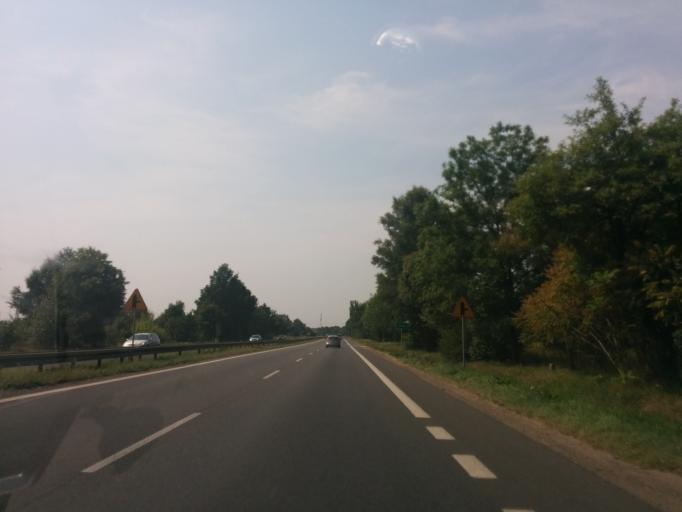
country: PL
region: Masovian Voivodeship
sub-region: Powiat pruszkowski
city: Nadarzyn
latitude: 52.0721
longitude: 20.7651
